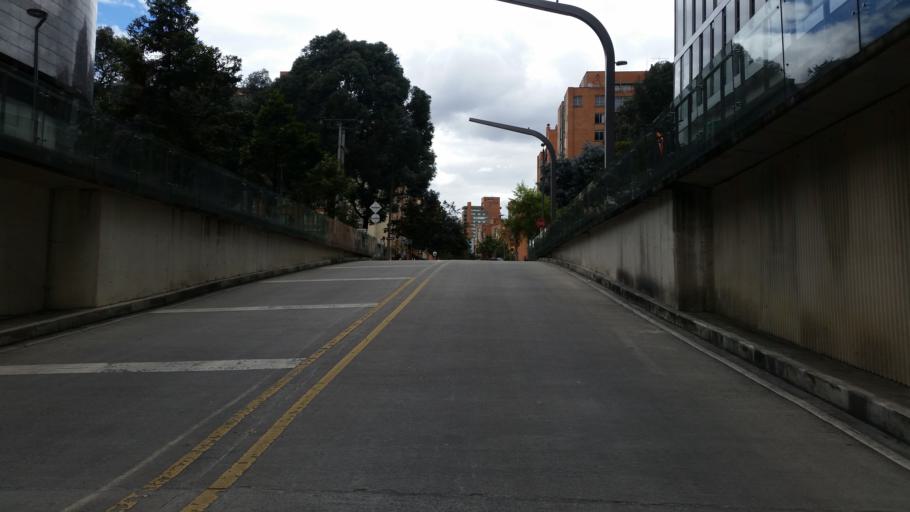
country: CO
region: Bogota D.C.
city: Bogota
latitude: 4.6449
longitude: -74.1001
